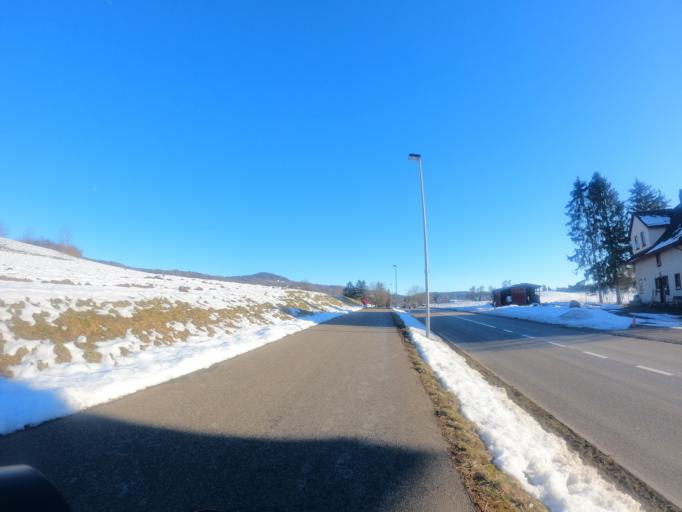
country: CH
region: Zurich
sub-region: Bezirk Affoltern
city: Affoltern / Unterdorf
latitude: 47.2849
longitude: 8.4436
